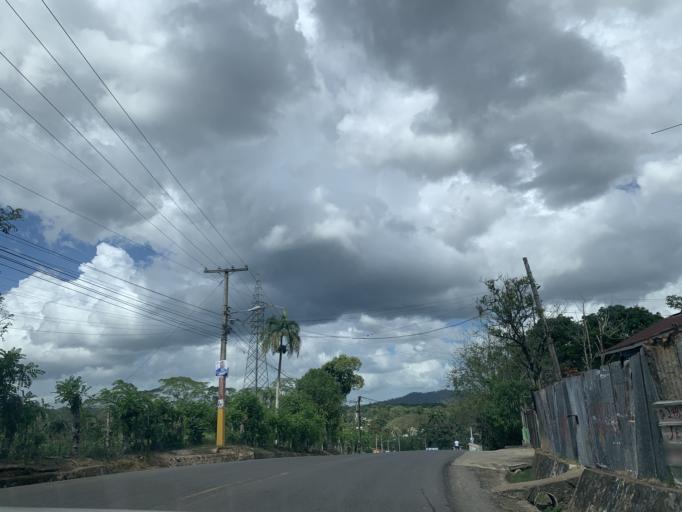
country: DO
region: Monte Plata
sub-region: Yamasa
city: Yamasa
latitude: 18.7617
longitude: -70.0193
